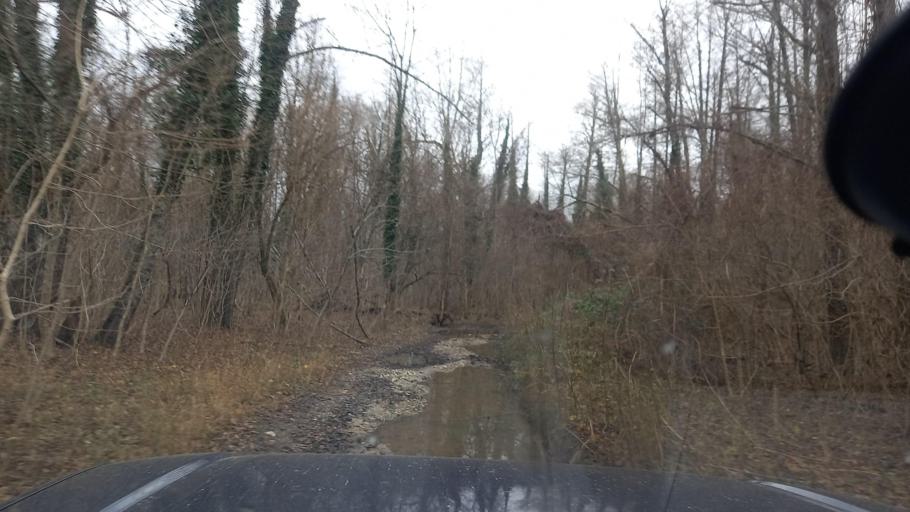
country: RU
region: Krasnodarskiy
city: Pshada
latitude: 44.4912
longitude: 38.4181
